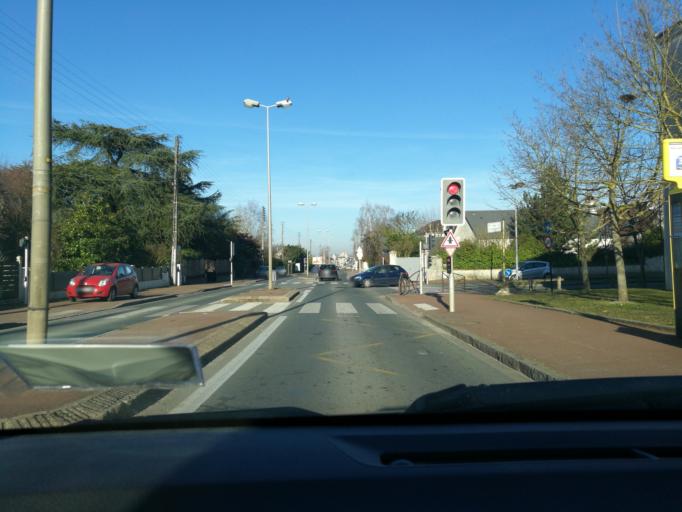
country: FR
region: Centre
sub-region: Departement du Loiret
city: Saint-Jean-de-la-Ruelle
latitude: 47.9177
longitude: 1.8606
